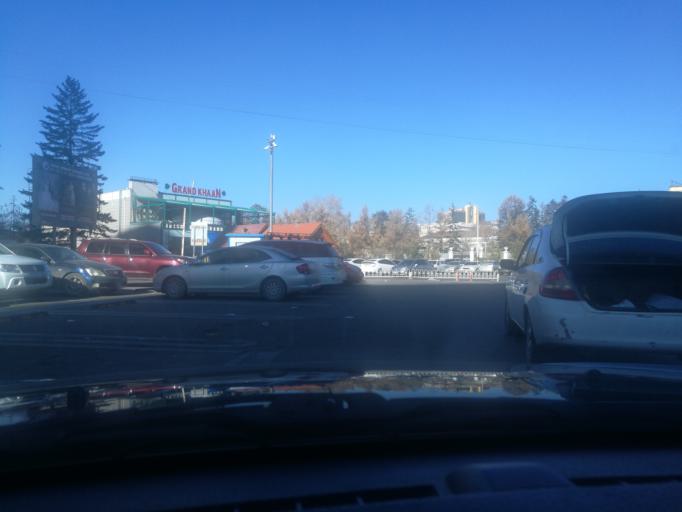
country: MN
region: Ulaanbaatar
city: Ulaanbaatar
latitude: 47.9150
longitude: 106.9149
